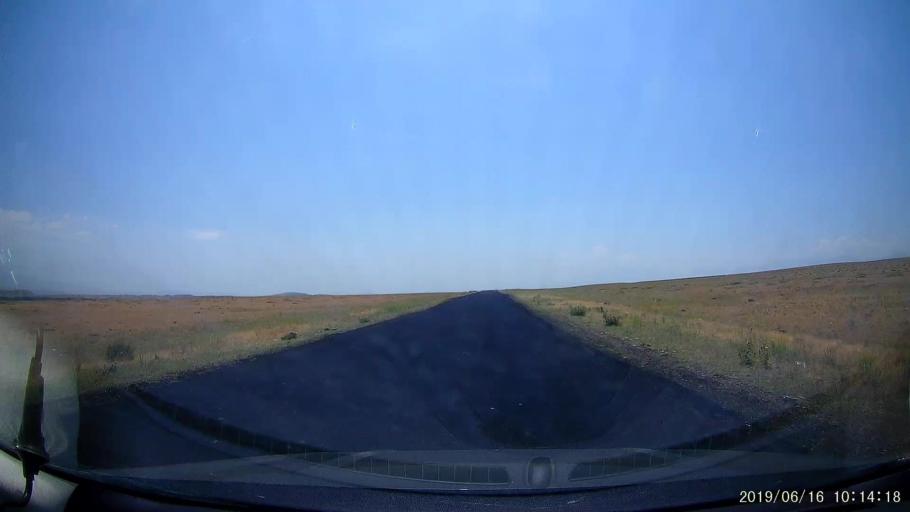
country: TR
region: Igdir
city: Tuzluca
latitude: 40.1861
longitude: 43.6598
